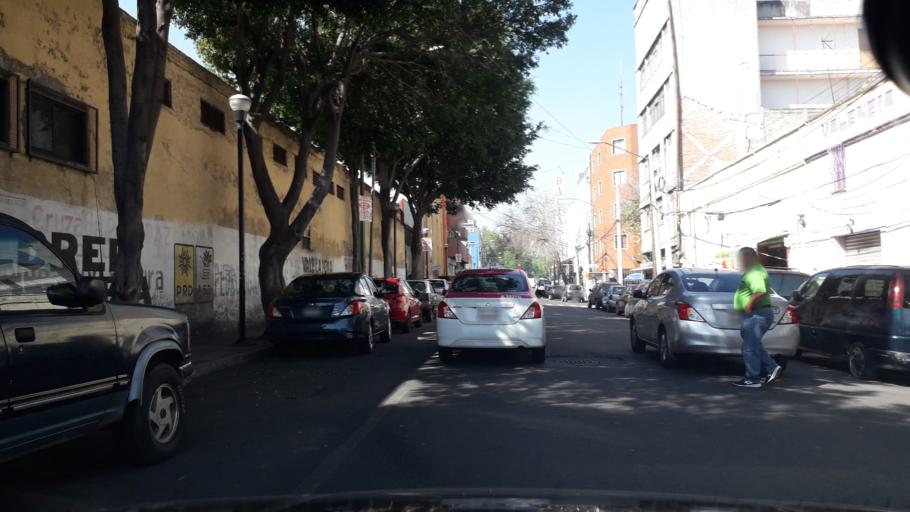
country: MX
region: Mexico City
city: Cuauhtemoc
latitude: 19.4403
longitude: -99.1503
